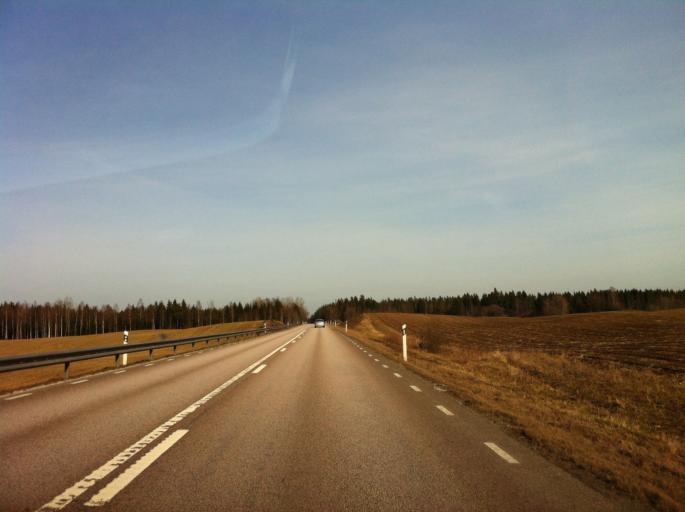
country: SE
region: Vaestra Goetaland
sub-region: Tidaholms Kommun
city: Tidaholm
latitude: 58.0746
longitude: 13.8648
